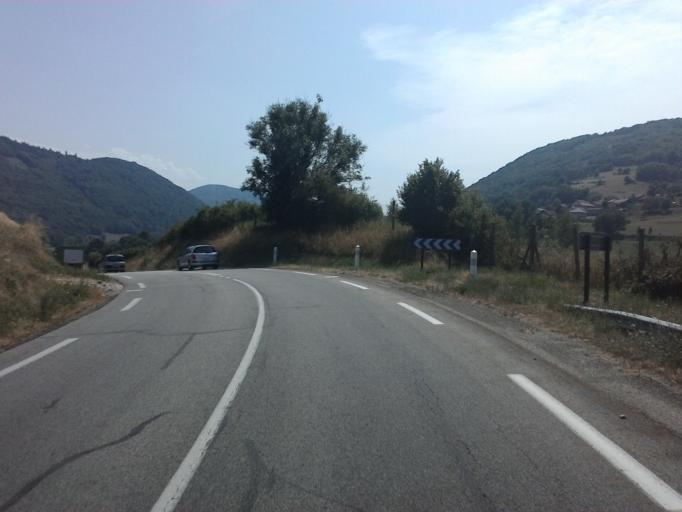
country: FR
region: Rhone-Alpes
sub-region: Departement de l'Isere
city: Bilieu
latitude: 45.4365
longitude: 5.5646
